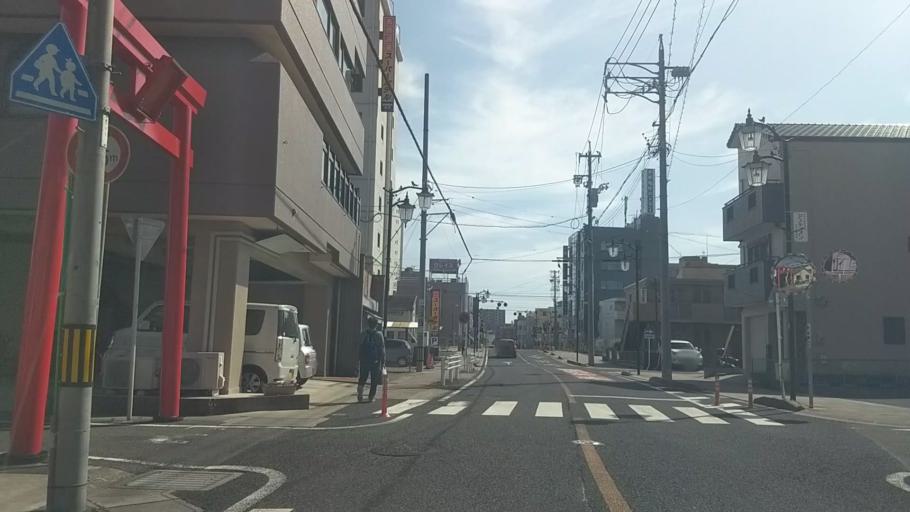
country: JP
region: Aichi
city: Anjo
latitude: 34.9604
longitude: 137.0893
